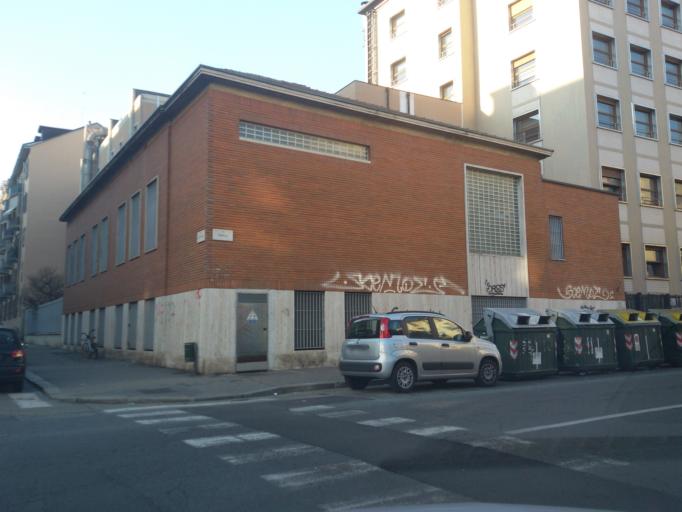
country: IT
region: Piedmont
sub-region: Provincia di Torino
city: Lesna
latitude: 45.0438
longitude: 7.6450
